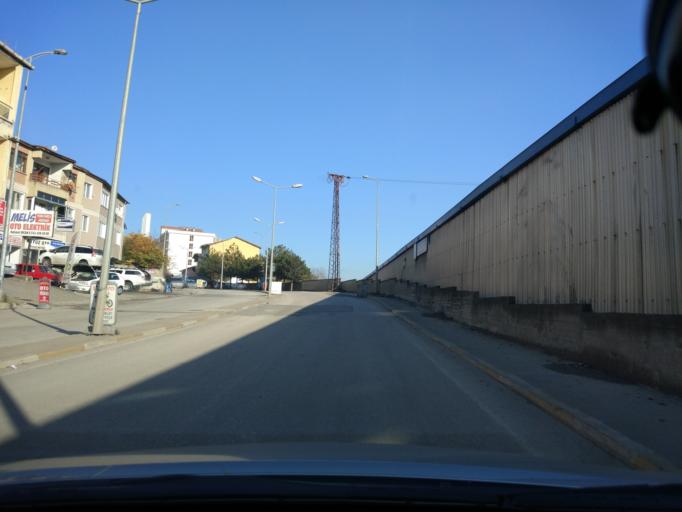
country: TR
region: Karabuk
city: Karabuk
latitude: 41.2072
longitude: 32.6375
